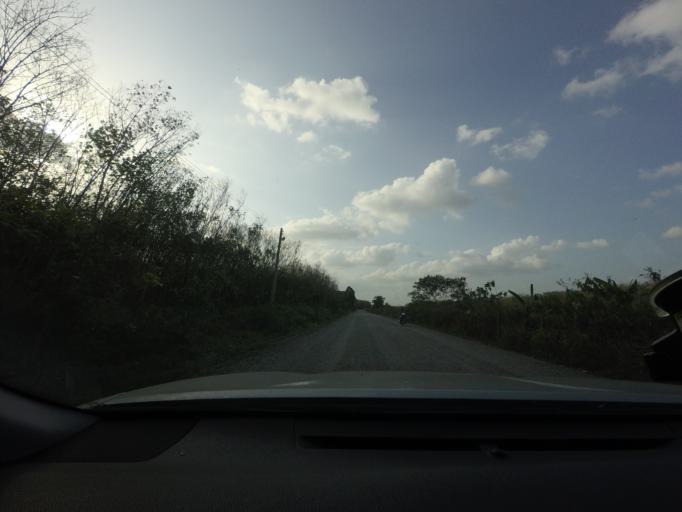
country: TH
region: Pattani
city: Mae Lan
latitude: 6.6190
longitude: 101.2524
